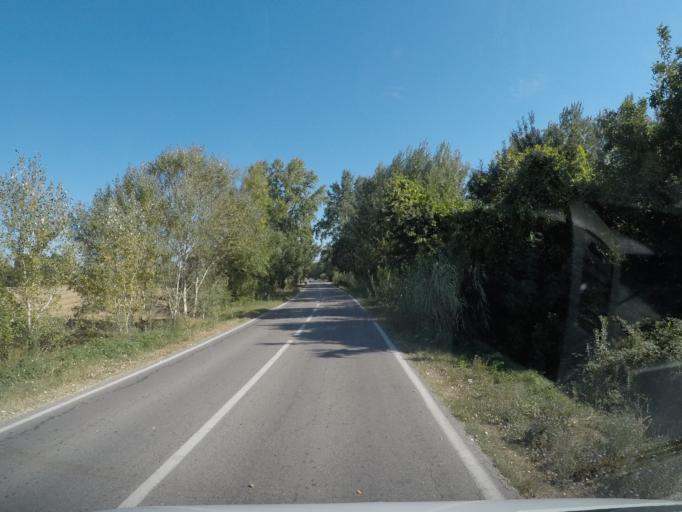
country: FR
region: Languedoc-Roussillon
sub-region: Departement du Gard
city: Moussac
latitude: 43.9705
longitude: 4.2223
